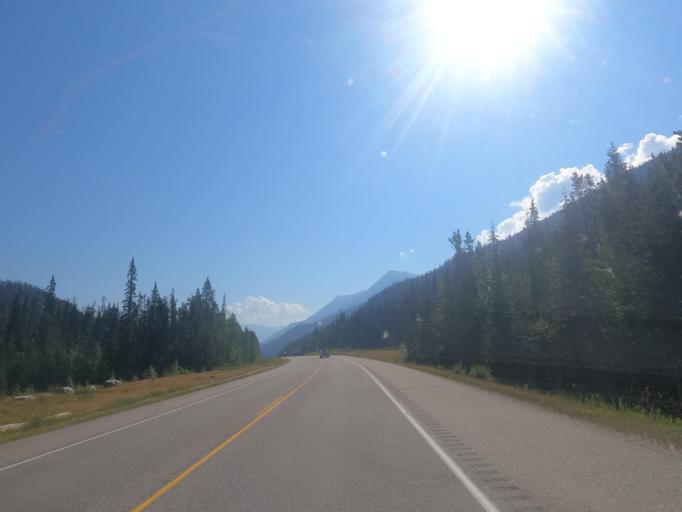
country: CA
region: Alberta
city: Jasper Park Lodge
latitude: 52.8682
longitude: -118.2611
